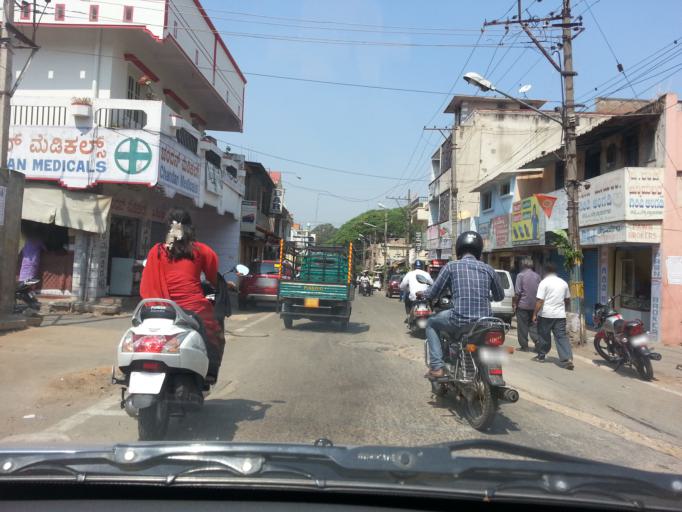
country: IN
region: Karnataka
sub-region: Mysore
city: Mysore
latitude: 12.3085
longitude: 76.6662
